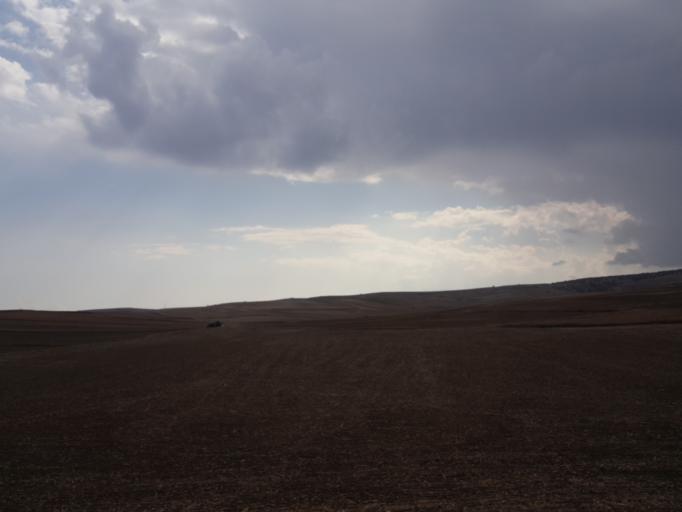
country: TR
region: Corum
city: Alaca
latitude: 40.1378
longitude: 34.7888
